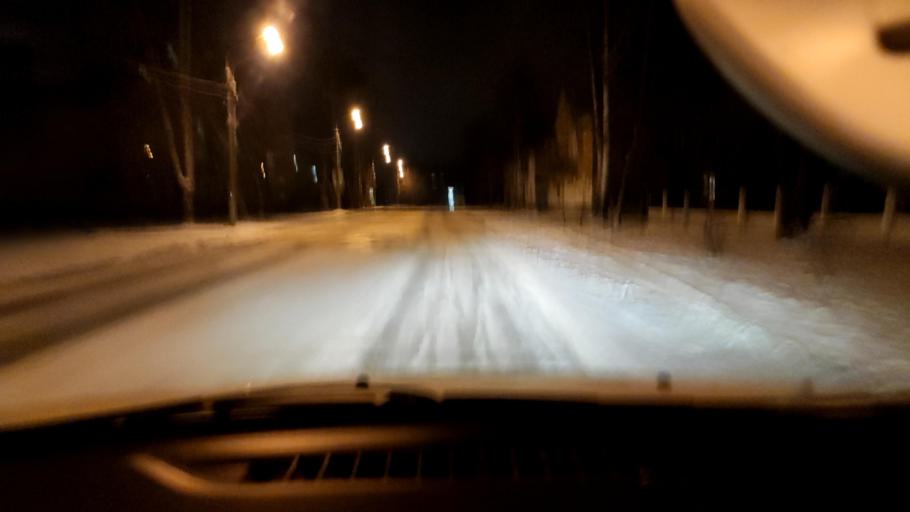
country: RU
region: Perm
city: Kultayevo
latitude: 58.0050
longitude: 55.9591
